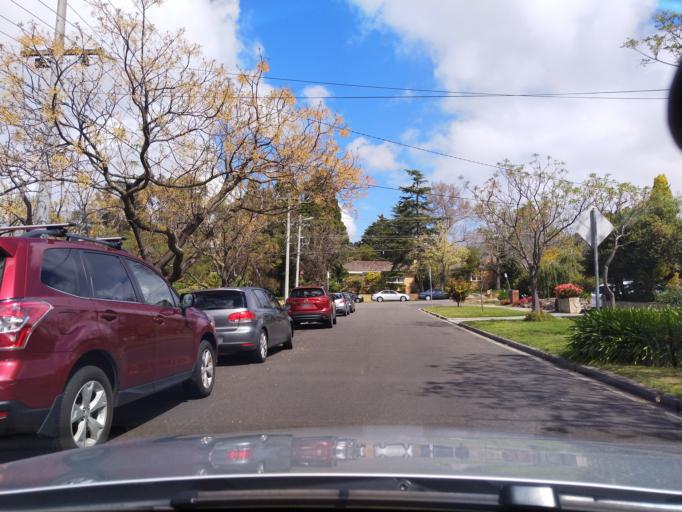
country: AU
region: Victoria
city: Rosanna
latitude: -37.7624
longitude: 145.0635
